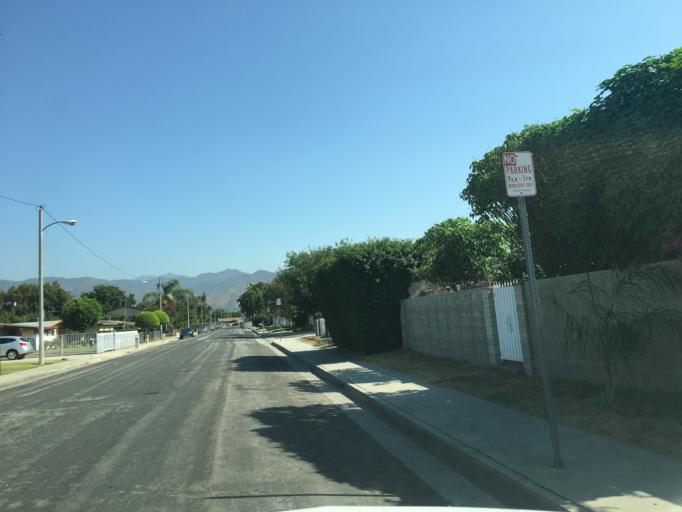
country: US
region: California
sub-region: Los Angeles County
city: Citrus
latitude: 34.1112
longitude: -117.9006
